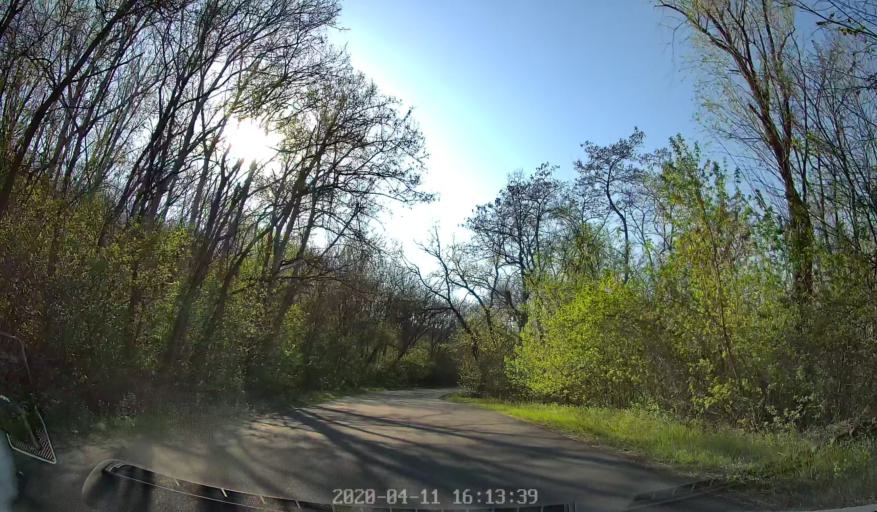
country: MD
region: Chisinau
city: Vadul lui Voda
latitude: 47.0726
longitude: 29.1092
